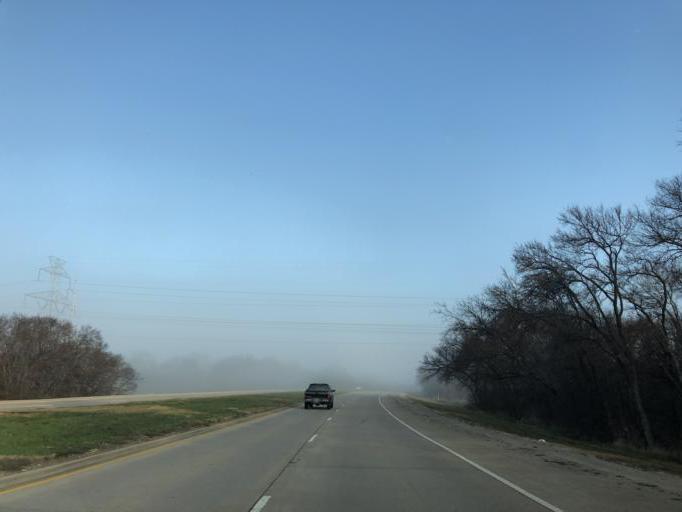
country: US
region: Texas
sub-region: Dallas County
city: Duncanville
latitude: 32.6652
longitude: -96.9841
